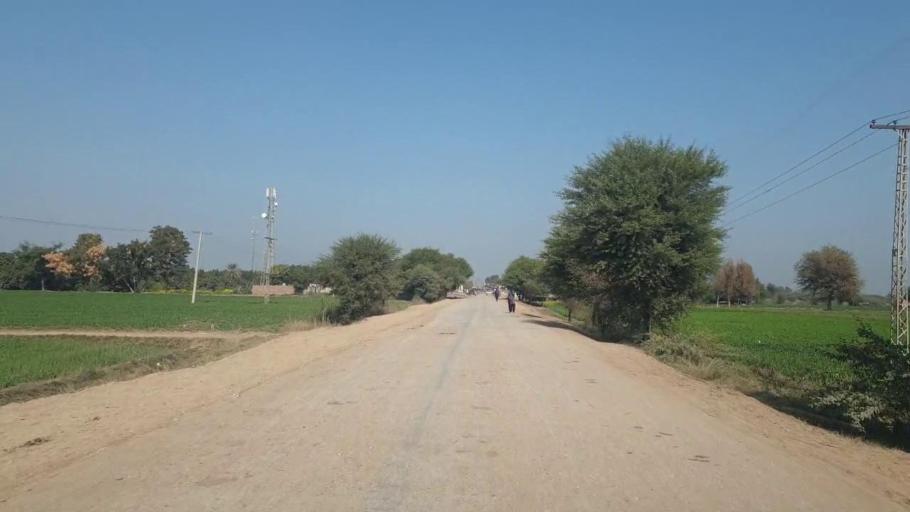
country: PK
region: Sindh
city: Sakrand
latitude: 26.0503
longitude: 68.4031
